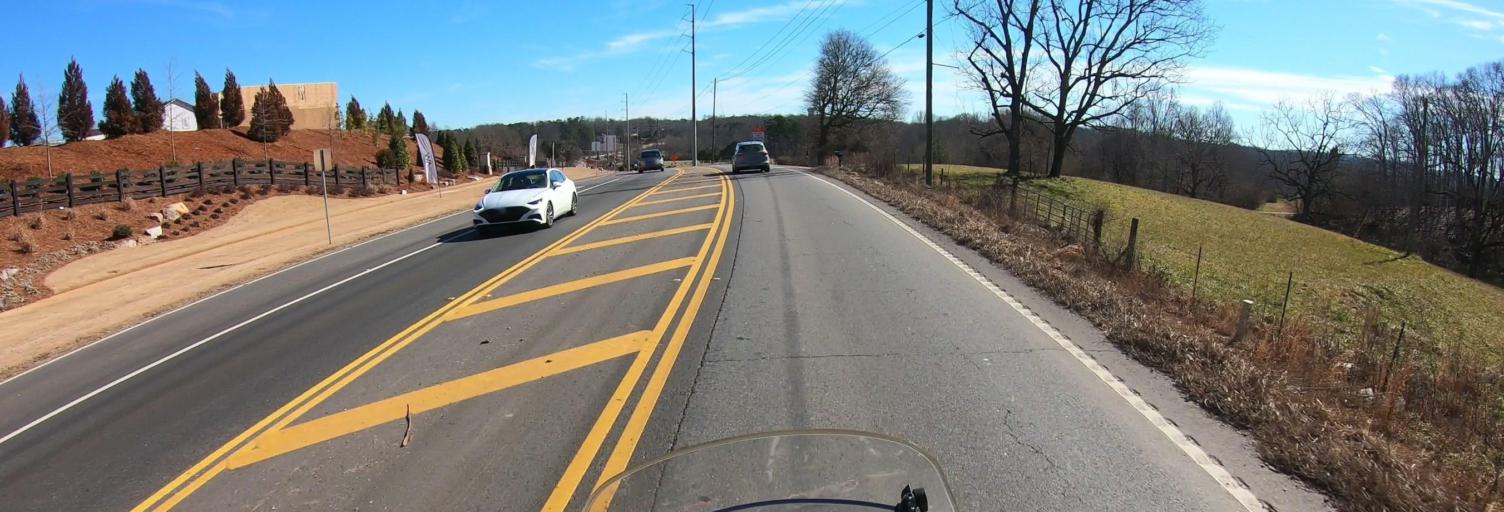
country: US
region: Georgia
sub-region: Forsyth County
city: Cumming
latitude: 34.2916
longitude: -84.1494
